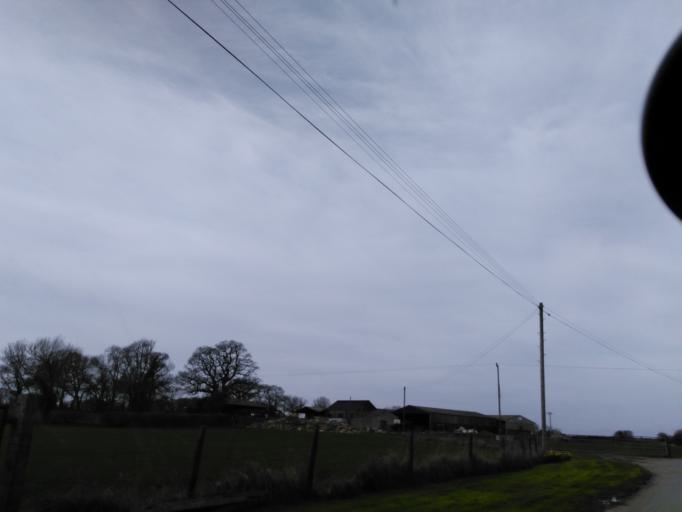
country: GB
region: England
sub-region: Wiltshire
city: Neston
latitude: 51.4345
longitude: -2.2099
